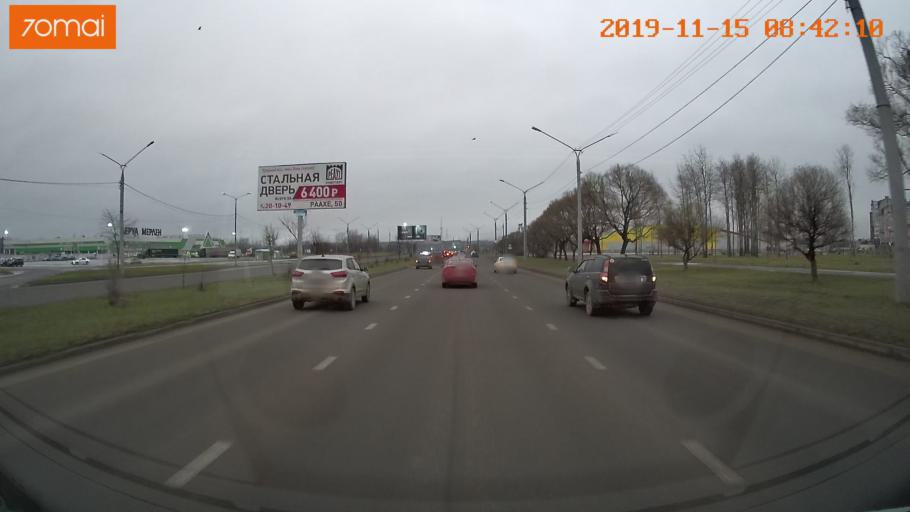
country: RU
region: Vologda
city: Cherepovets
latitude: 59.1009
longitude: 37.9094
